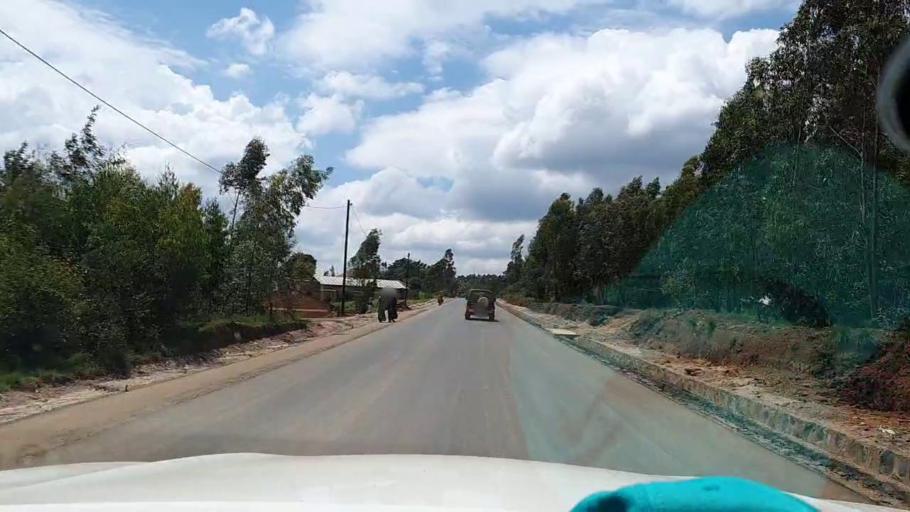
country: RW
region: Southern Province
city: Nzega
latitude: -2.6561
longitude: 29.5602
